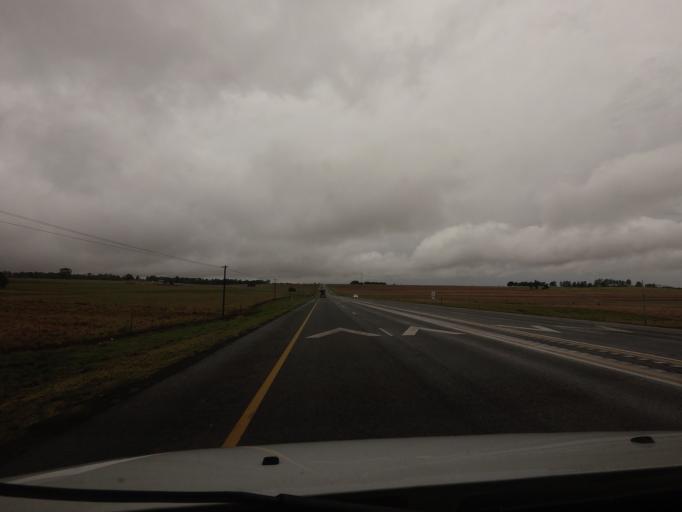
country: ZA
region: Mpumalanga
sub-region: Nkangala District Municipality
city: Belfast
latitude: -25.7777
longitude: 29.9412
